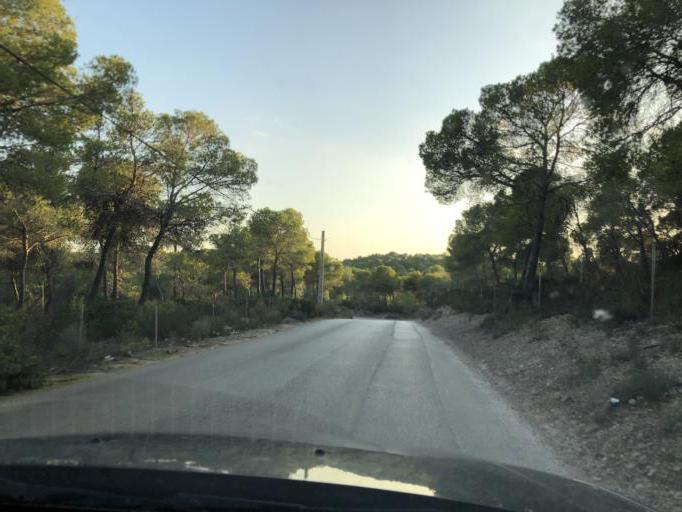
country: ES
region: Balearic Islands
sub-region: Illes Balears
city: Santa Ponsa
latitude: 39.5343
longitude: 2.4804
